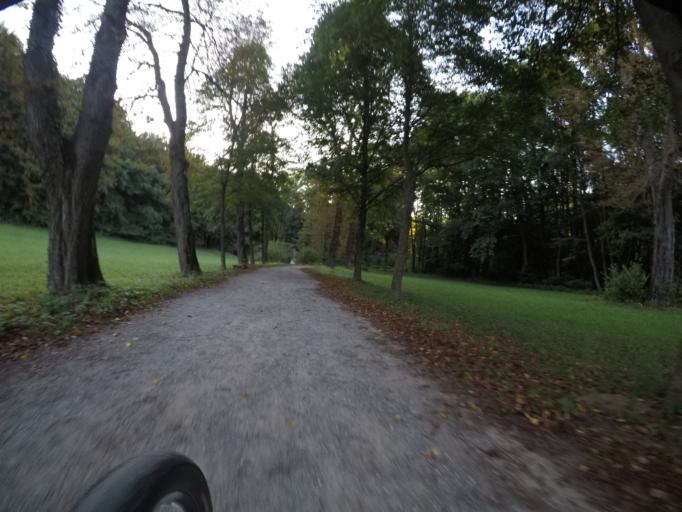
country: AT
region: Lower Austria
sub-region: Politischer Bezirk Bruck an der Leitha
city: Mannersdorf am Leithagebirge
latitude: 47.9547
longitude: 16.5972
